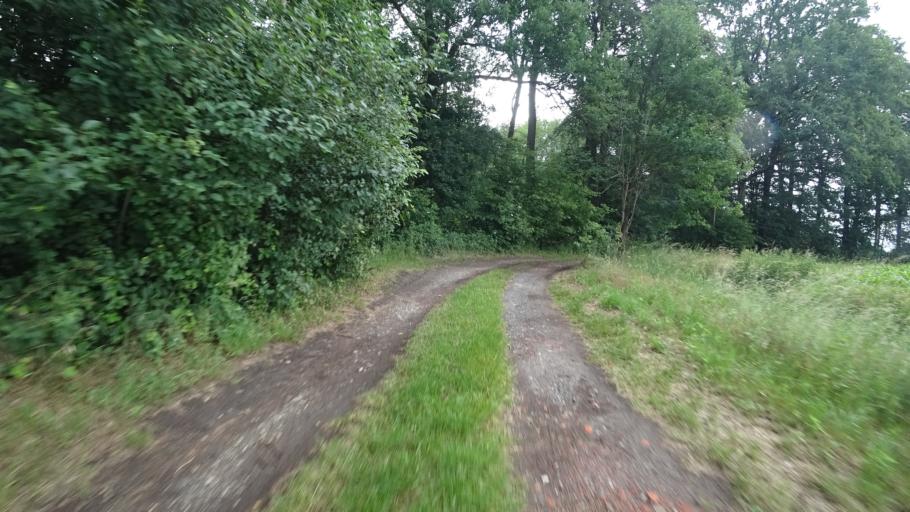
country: DE
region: North Rhine-Westphalia
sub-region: Regierungsbezirk Detmold
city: Guetersloh
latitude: 51.9459
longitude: 8.3277
